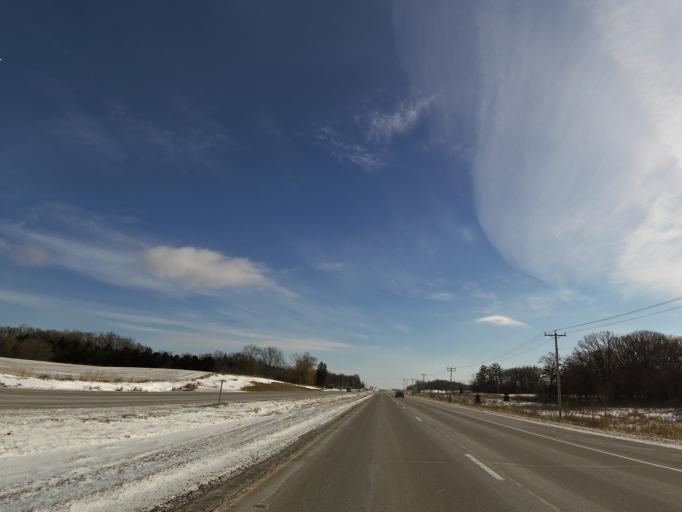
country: US
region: Minnesota
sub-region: Dakota County
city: Rosemount
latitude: 44.7389
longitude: -93.0603
